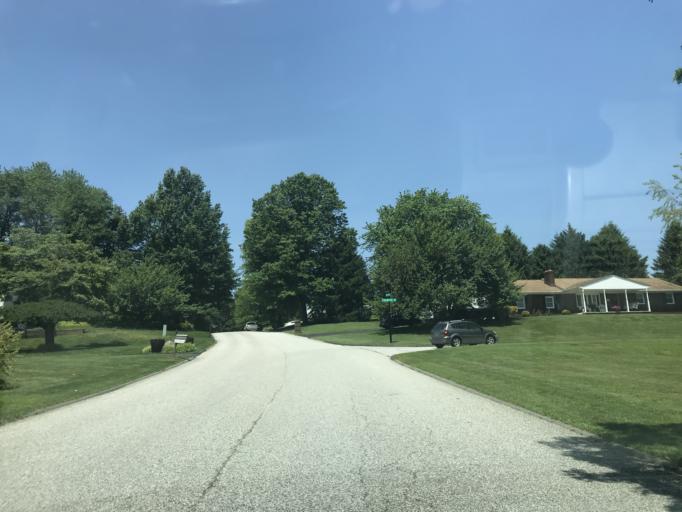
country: US
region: Maryland
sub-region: Harford County
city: South Bel Air
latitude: 39.5579
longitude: -76.2686
